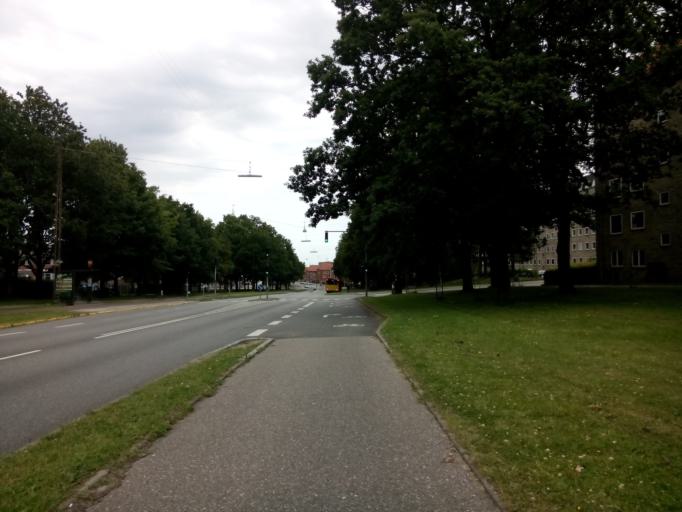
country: DK
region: Central Jutland
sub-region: Arhus Kommune
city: Arhus
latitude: 56.1734
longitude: 10.1827
